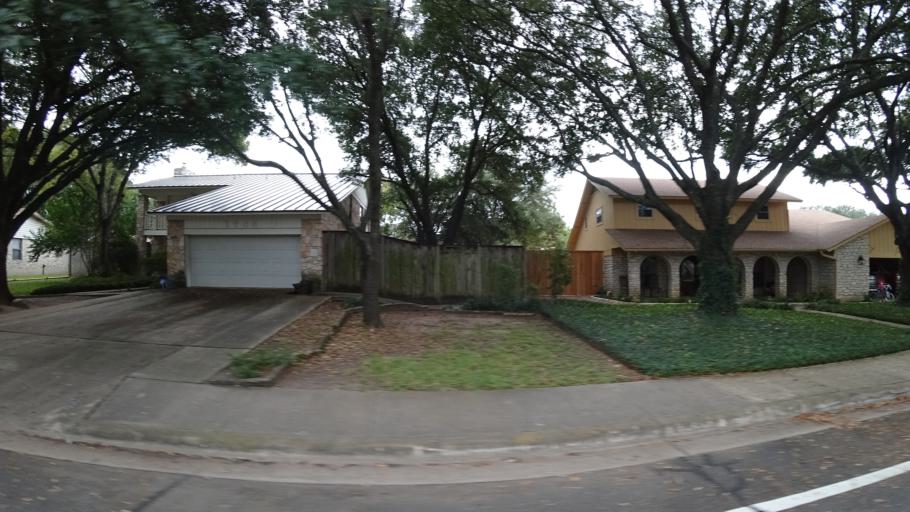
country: US
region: Texas
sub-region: Williamson County
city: Round Rock
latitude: 30.4973
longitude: -97.7008
